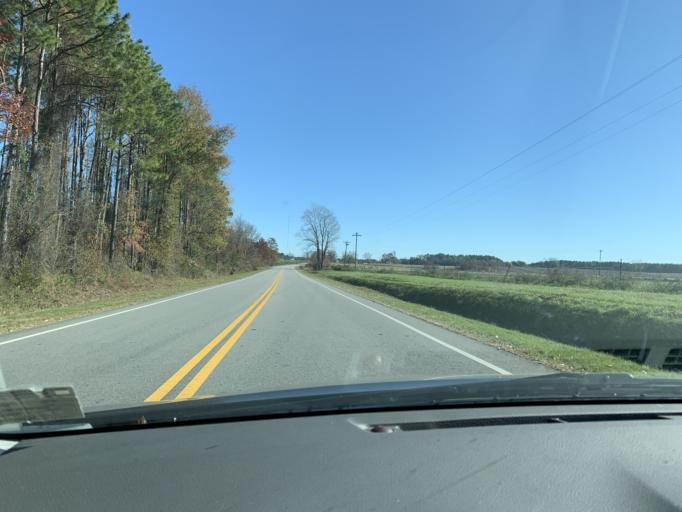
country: US
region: Georgia
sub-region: Ben Hill County
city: Fitzgerald
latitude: 31.7135
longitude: -83.1854
